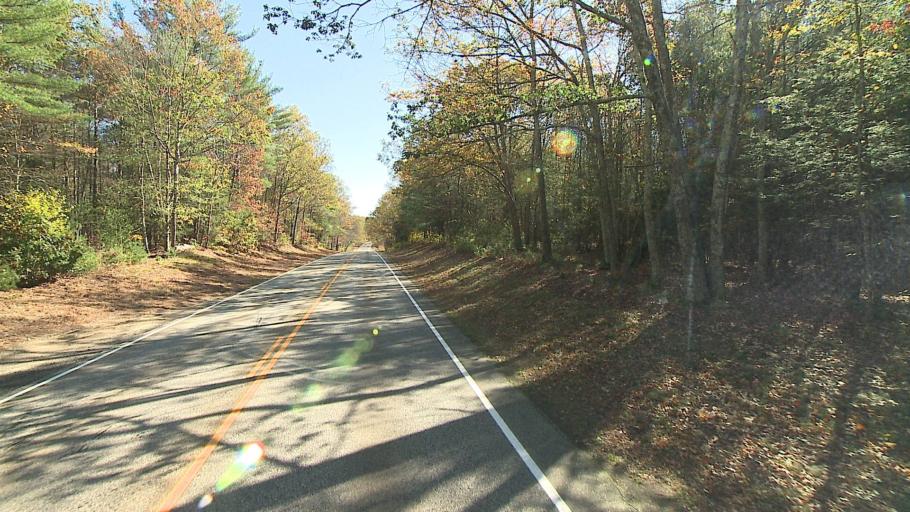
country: US
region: Connecticut
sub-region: Windham County
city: South Woodstock
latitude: 41.8710
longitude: -72.0586
